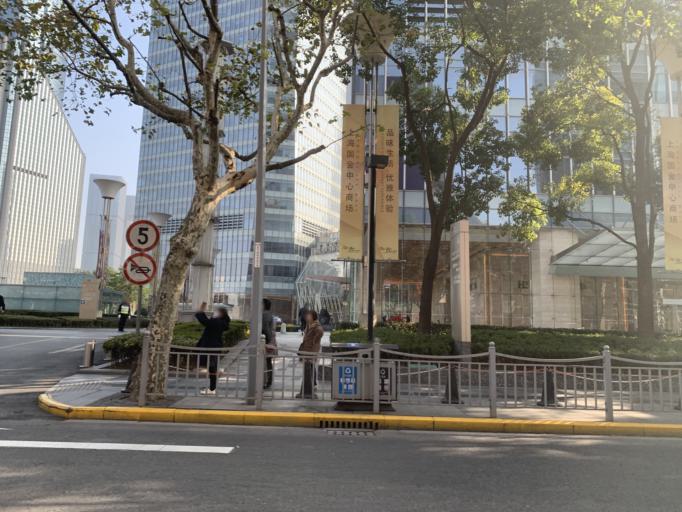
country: CN
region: Shanghai Shi
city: Hongkou
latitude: 31.2388
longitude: 121.4962
